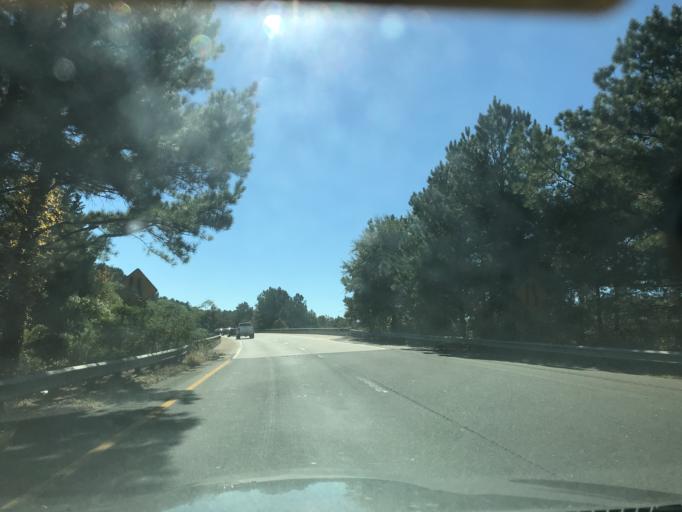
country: US
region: North Carolina
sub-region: Wake County
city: Morrisville
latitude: 35.9046
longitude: -78.8716
